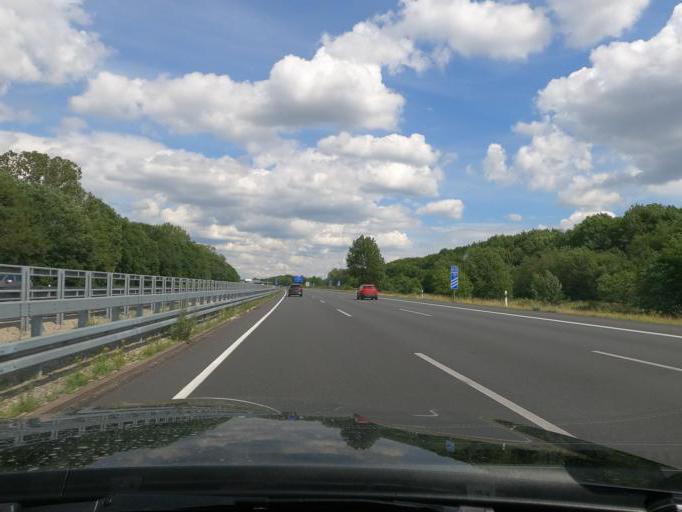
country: DE
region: Lower Saxony
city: Langenhagen
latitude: 52.4268
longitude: 9.7651
